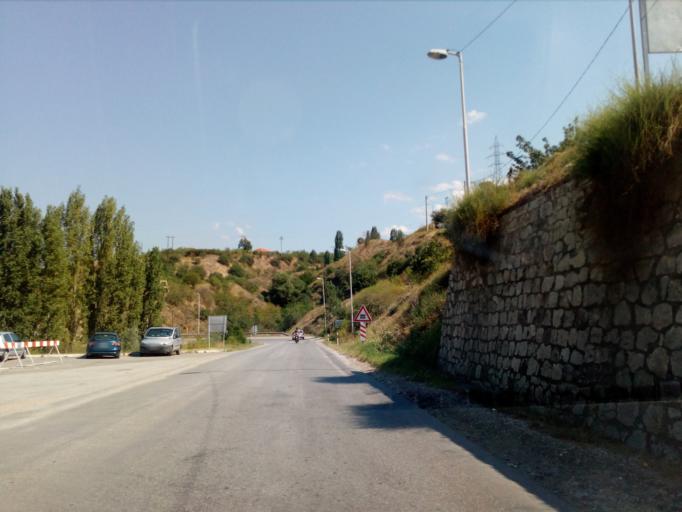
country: MK
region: Veles
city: Veles
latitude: 41.7237
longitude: 21.7872
